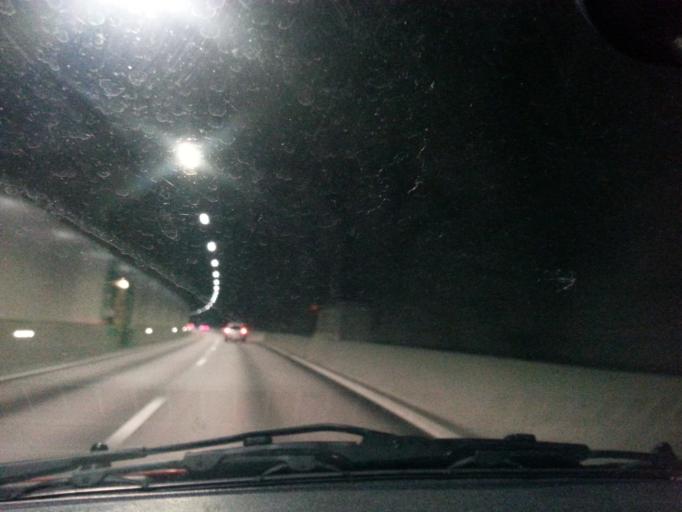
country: SE
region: Vaestra Goetaland
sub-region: Goteborg
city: Majorna
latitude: 57.6696
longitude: 11.8909
